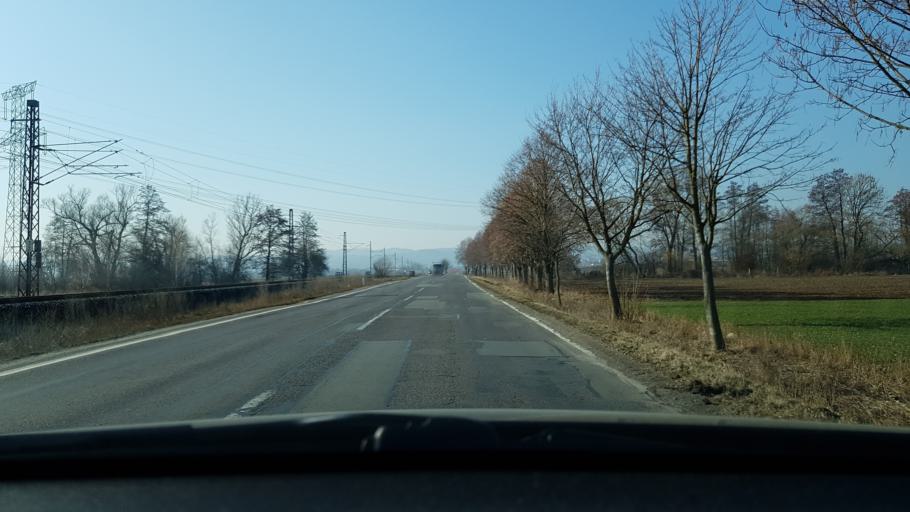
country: CZ
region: Olomoucky
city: Postrelmov
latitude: 49.8977
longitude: 16.9041
